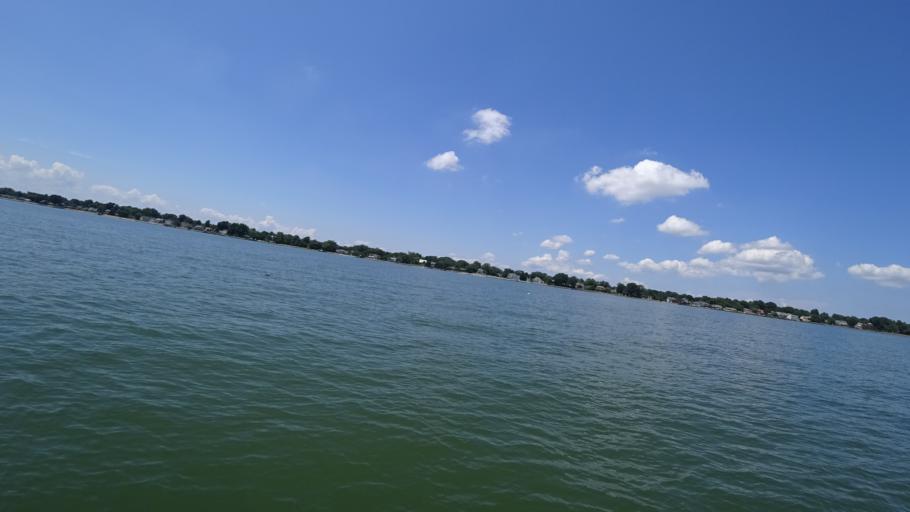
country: US
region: Virginia
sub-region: City of Hampton
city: Hampton
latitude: 36.9926
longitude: -76.3731
